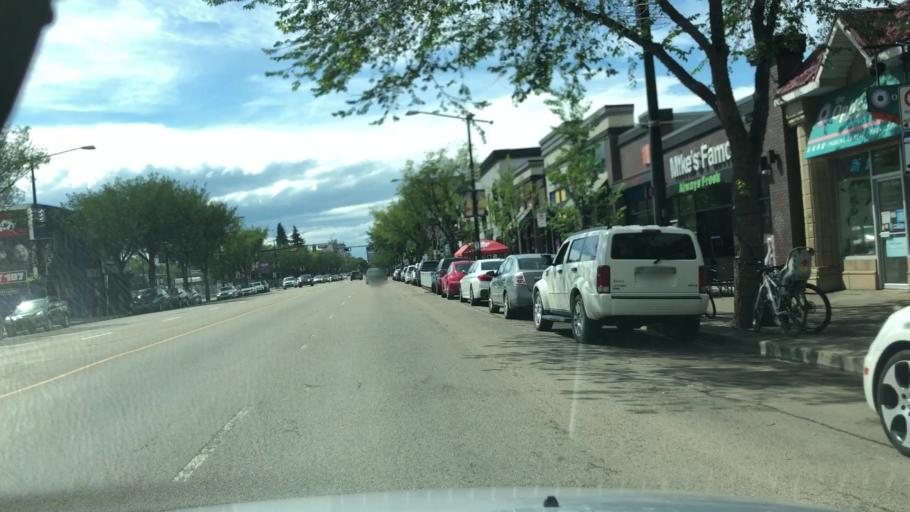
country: CA
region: Alberta
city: Edmonton
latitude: 53.5181
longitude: -113.5012
